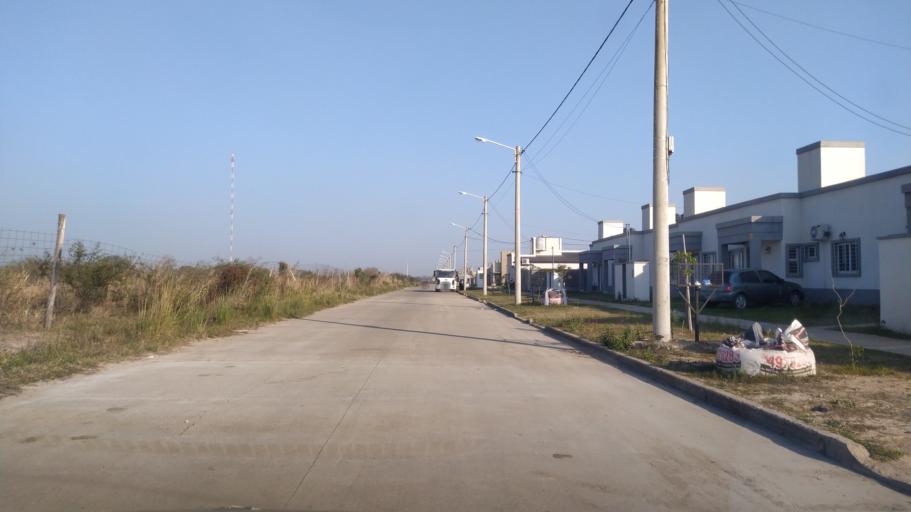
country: AR
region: Corrientes
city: Corrientes
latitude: -27.5285
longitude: -58.8041
